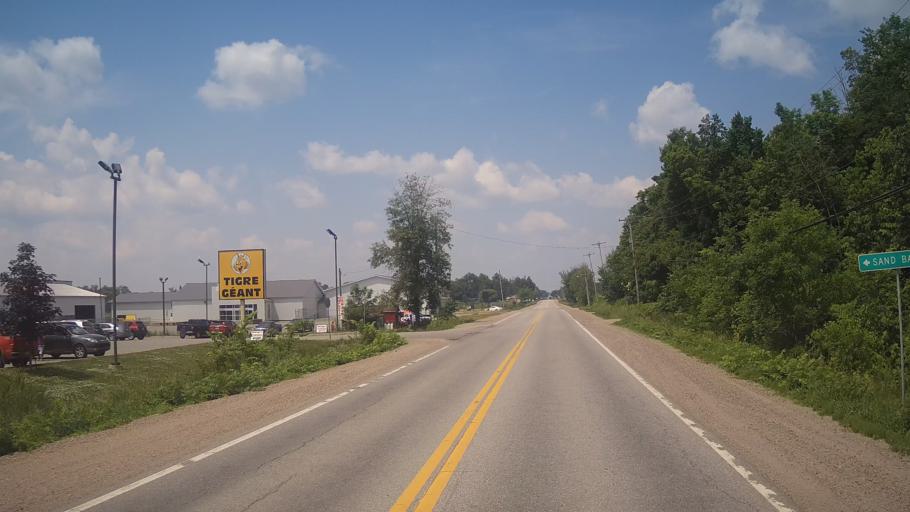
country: CA
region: Quebec
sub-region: Outaouais
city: Shawville
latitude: 45.6025
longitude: -76.5014
